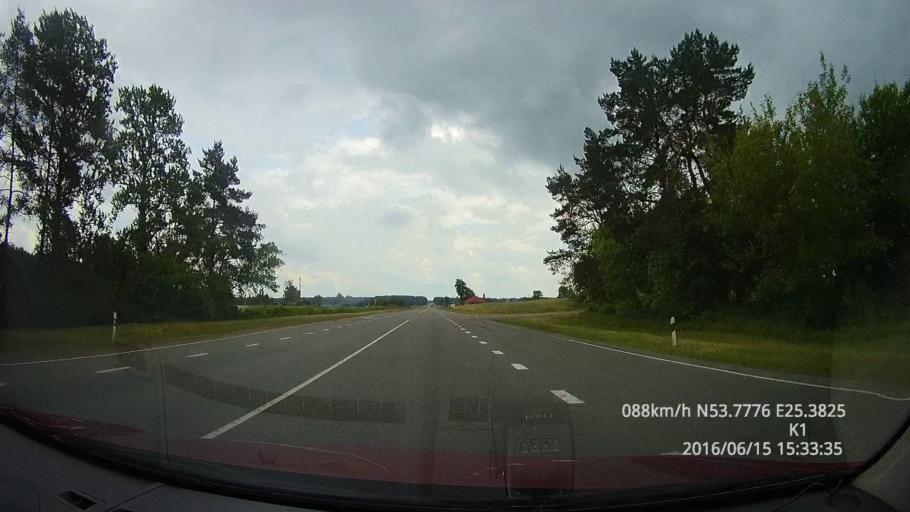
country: BY
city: Berezovka
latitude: 53.7768
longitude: 25.3829
